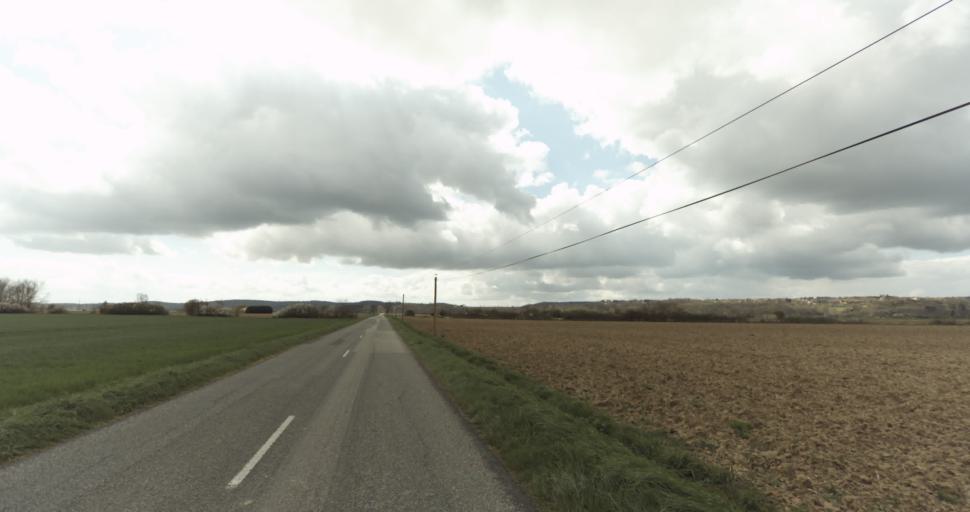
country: FR
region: Midi-Pyrenees
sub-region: Departement de la Haute-Garonne
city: Auterive
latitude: 43.3179
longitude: 1.4748
